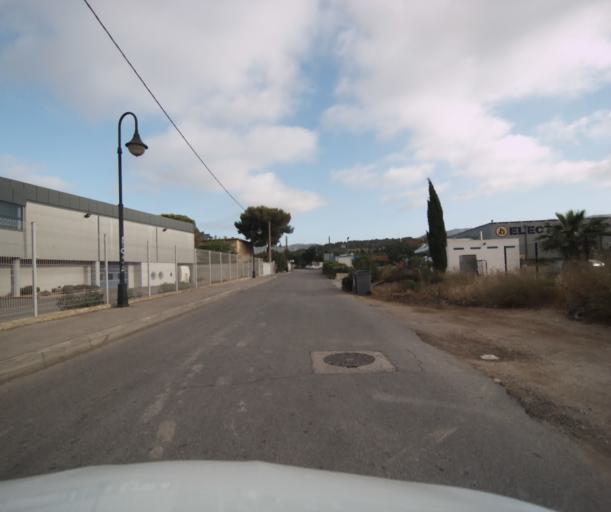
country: FR
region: Provence-Alpes-Cote d'Azur
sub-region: Departement du Var
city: Six-Fours-les-Plages
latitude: 43.1160
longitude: 5.8545
